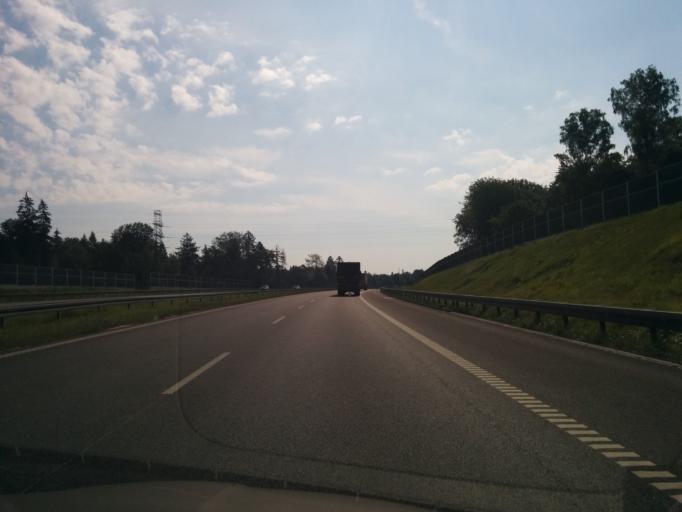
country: PL
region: Silesian Voivodeship
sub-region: Powiat tarnogorski
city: Tarnowskie Gory
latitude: 50.3875
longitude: 18.8414
